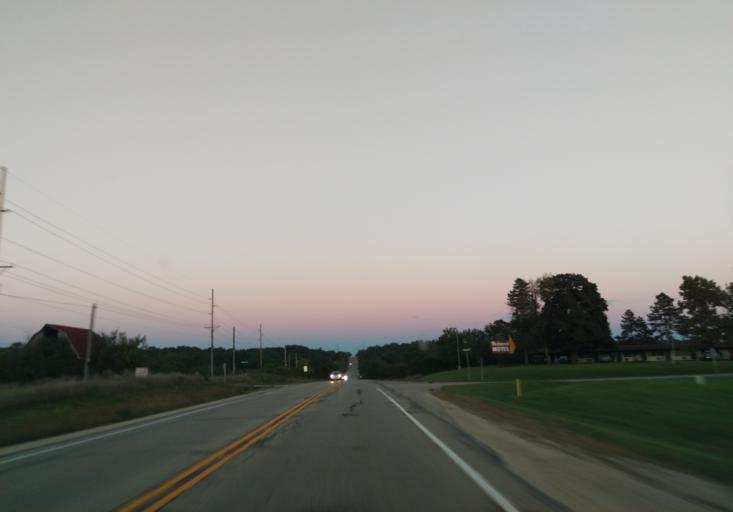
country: US
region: Wisconsin
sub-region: Rock County
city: Janesville
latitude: 42.7301
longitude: -89.0649
